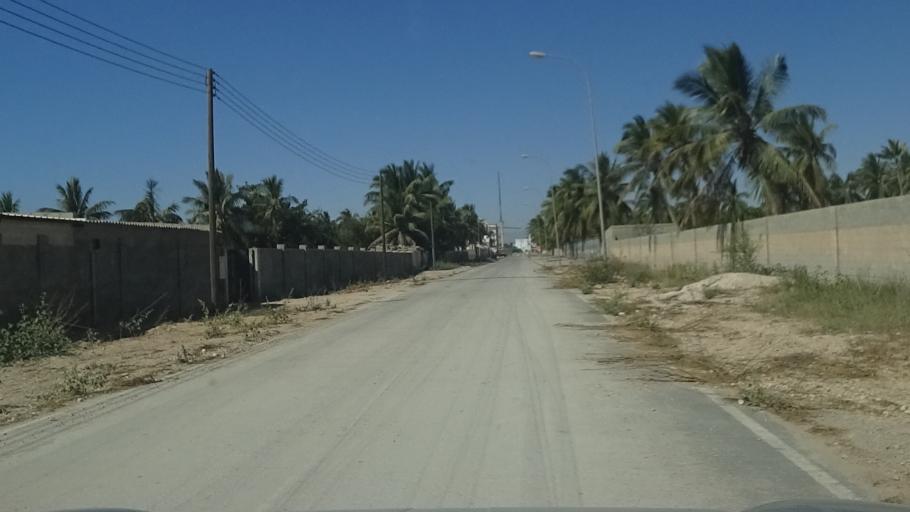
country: OM
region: Zufar
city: Salalah
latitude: 17.0288
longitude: 54.1645
